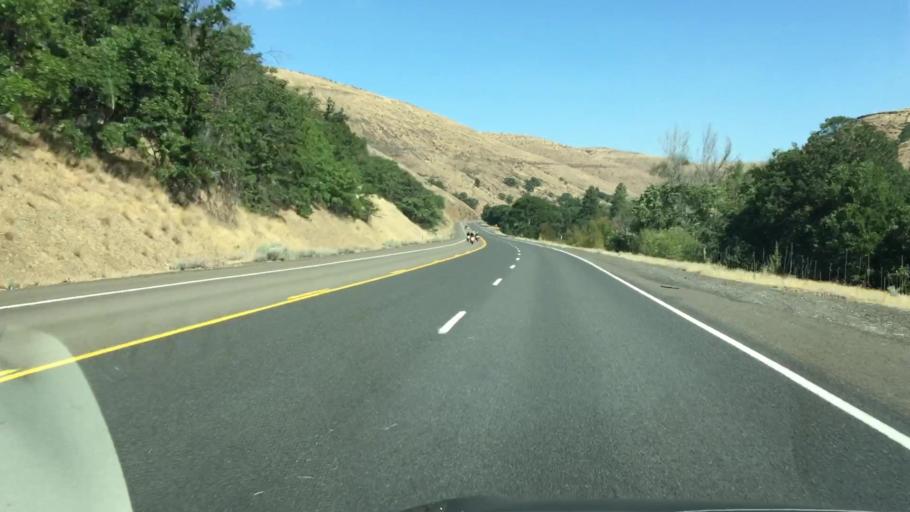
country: US
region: Oregon
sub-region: Wasco County
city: The Dalles
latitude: 45.2710
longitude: -121.1895
